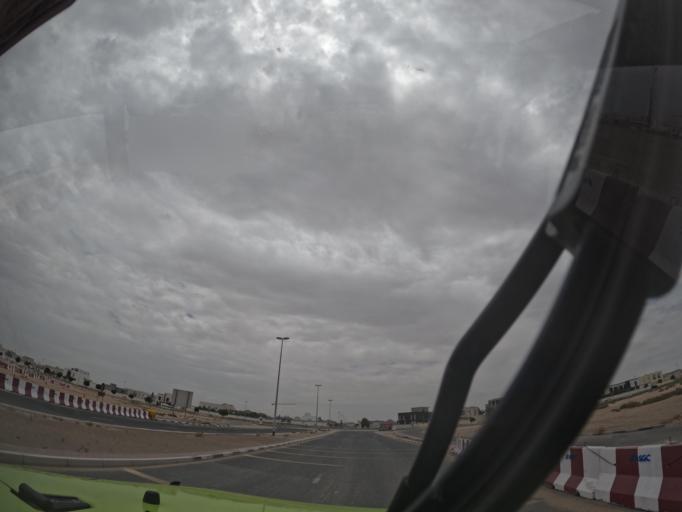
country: AE
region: Ash Shariqah
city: Sharjah
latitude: 25.1488
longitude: 55.3550
